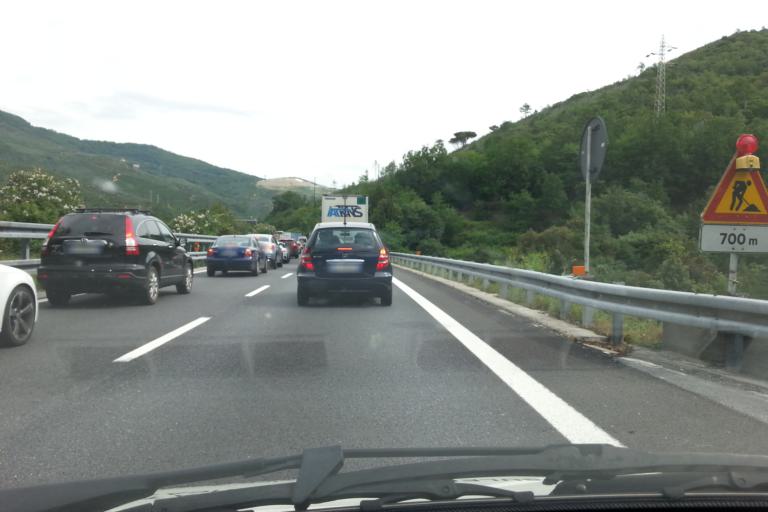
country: IT
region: Liguria
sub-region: Provincia di Savona
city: Valle di Vado
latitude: 44.2514
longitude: 8.4066
